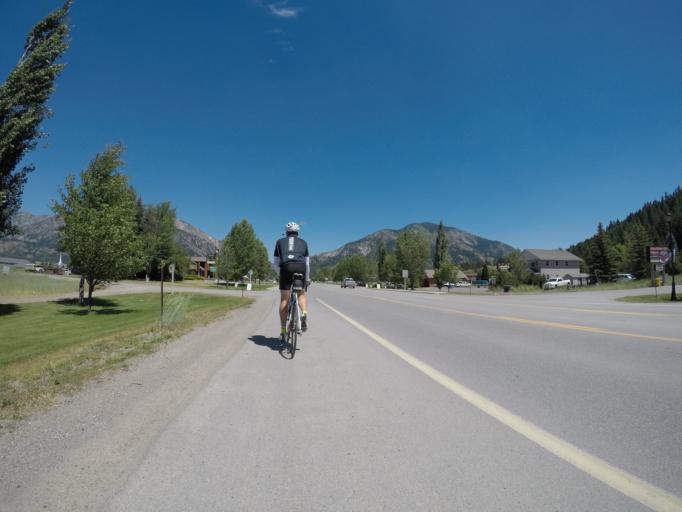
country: US
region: Wyoming
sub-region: Teton County
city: Hoback
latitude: 43.1612
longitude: -111.0237
